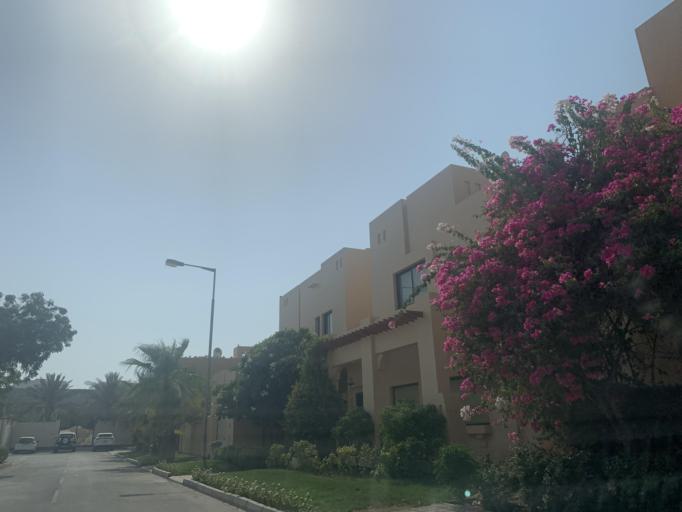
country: BH
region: Manama
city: Jidd Hafs
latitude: 26.2060
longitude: 50.4926
